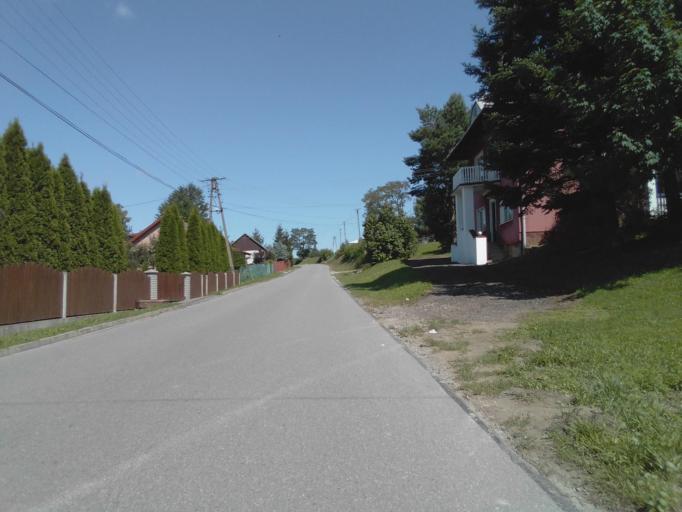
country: PL
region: Subcarpathian Voivodeship
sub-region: Powiat krosnienski
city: Jedlicze
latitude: 49.6673
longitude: 21.6120
